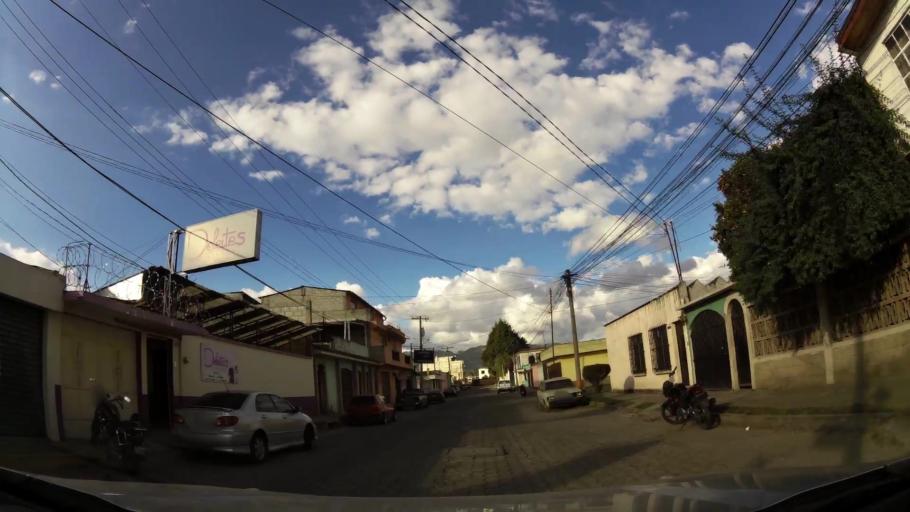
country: GT
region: Quetzaltenango
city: Quetzaltenango
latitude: 14.8521
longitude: -91.5280
